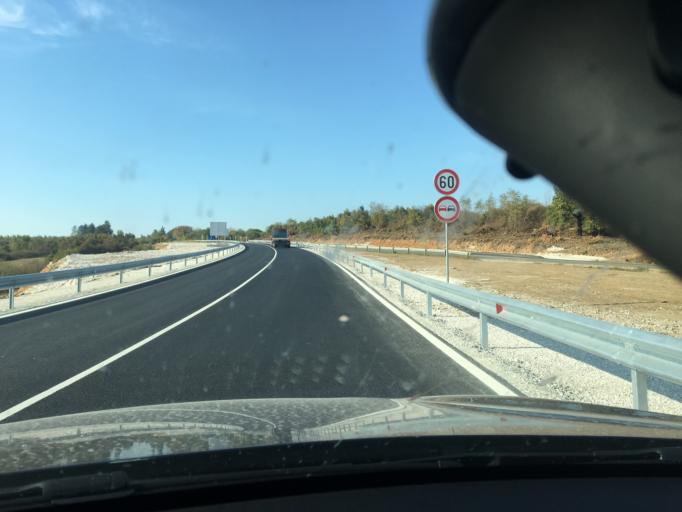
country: BG
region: Lovech
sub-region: Obshtina Yablanitsa
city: Yablanitsa
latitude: 43.0569
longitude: 24.2220
